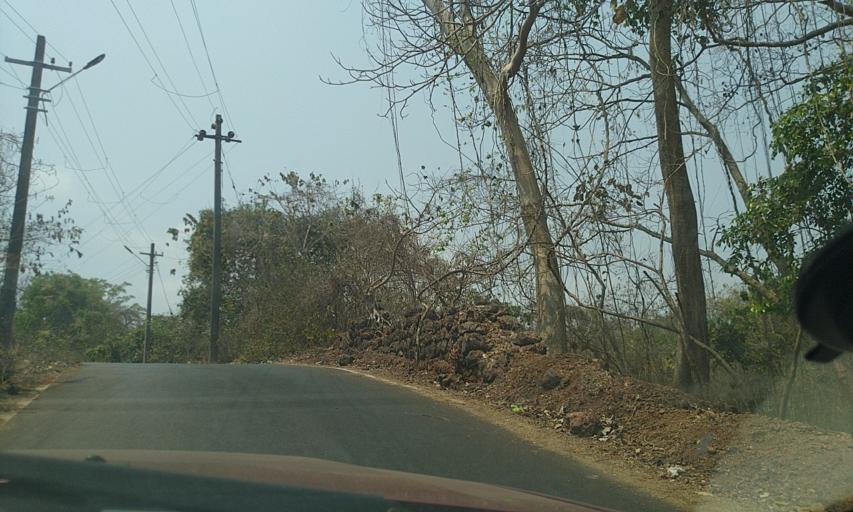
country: IN
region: Goa
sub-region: North Goa
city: Serula
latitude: 15.5236
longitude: 73.8402
